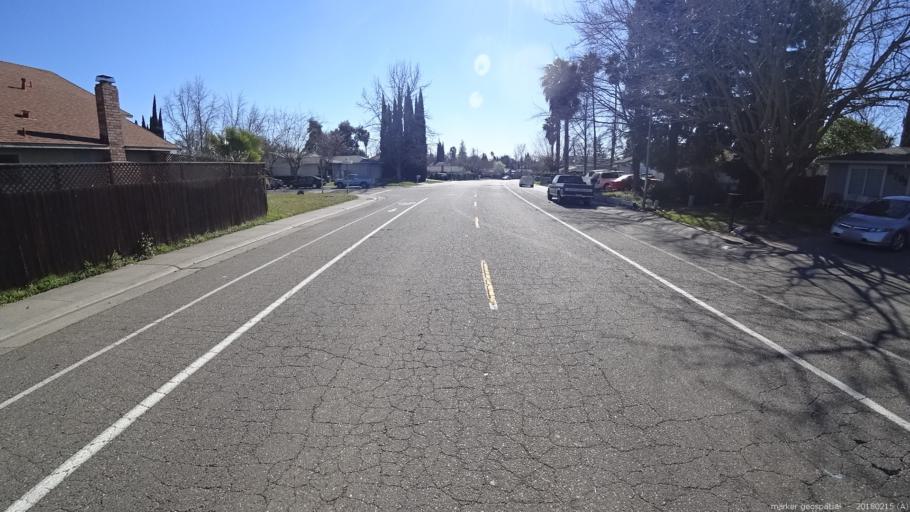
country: US
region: California
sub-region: Sacramento County
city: Antelope
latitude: 38.6968
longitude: -121.3311
